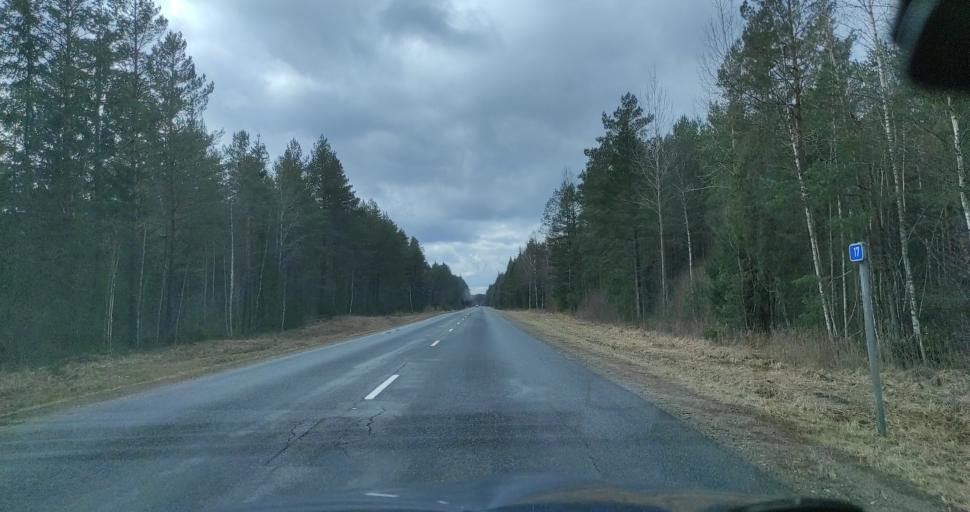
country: LV
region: Talsu Rajons
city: Stende
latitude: 57.1121
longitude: 22.5038
